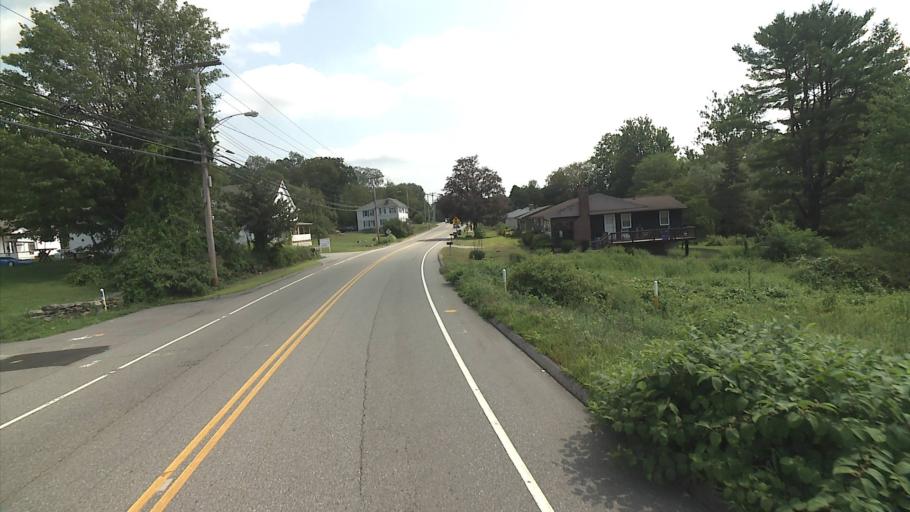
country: US
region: Connecticut
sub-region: New London County
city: Montville Center
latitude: 41.5074
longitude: -72.1251
